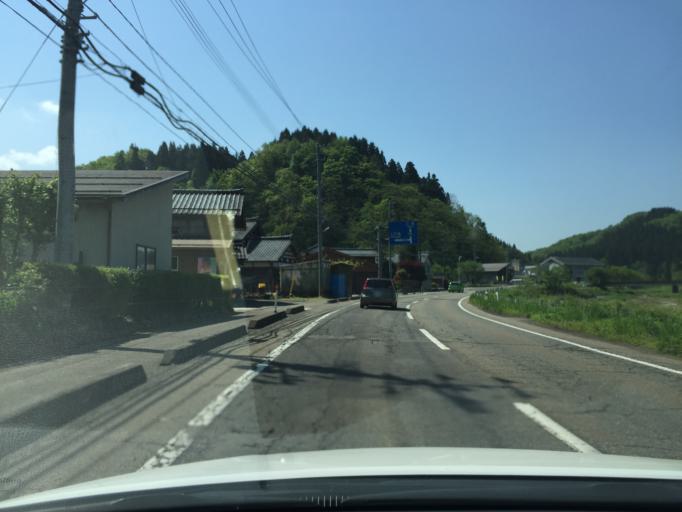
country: JP
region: Niigata
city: Kamo
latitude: 37.6186
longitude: 139.1043
